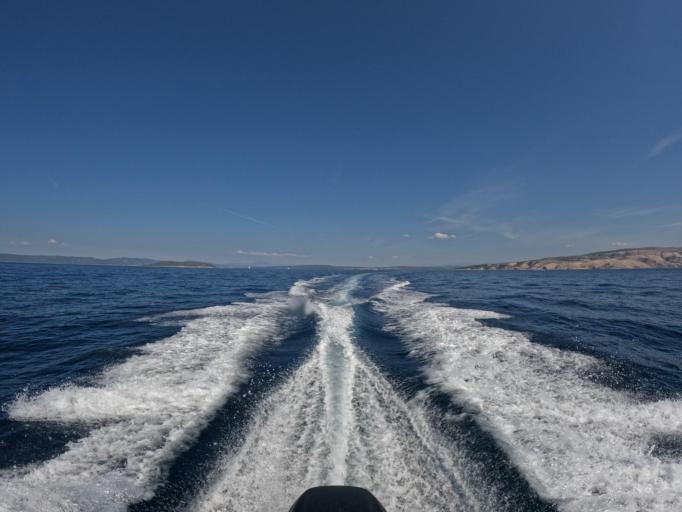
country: HR
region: Primorsko-Goranska
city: Punat
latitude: 44.9213
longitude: 14.6213
